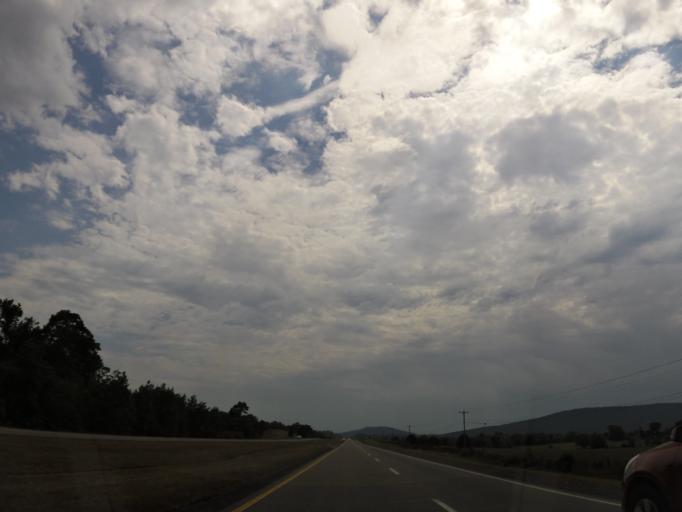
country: US
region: Alabama
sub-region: Jackson County
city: Bridgeport
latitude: 34.9328
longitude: -85.7633
